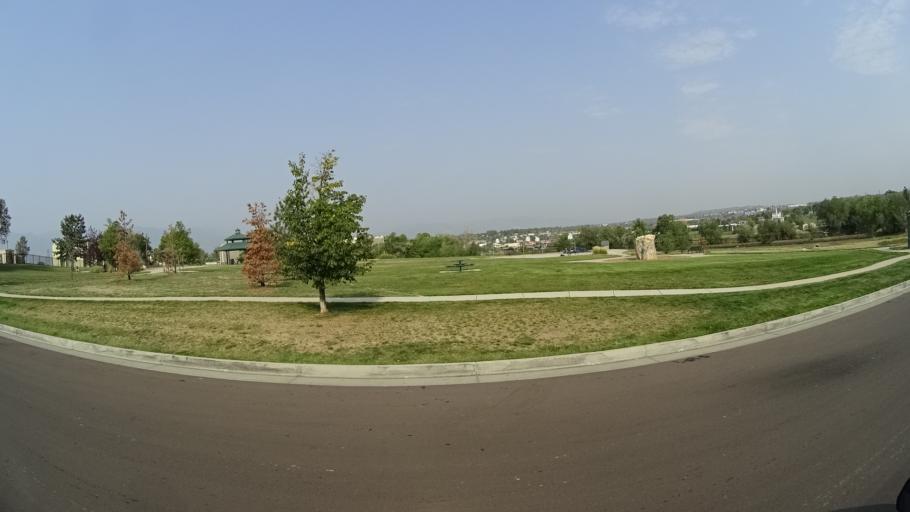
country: US
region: Colorado
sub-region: El Paso County
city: Stratmoor
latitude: 38.8207
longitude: -104.7528
